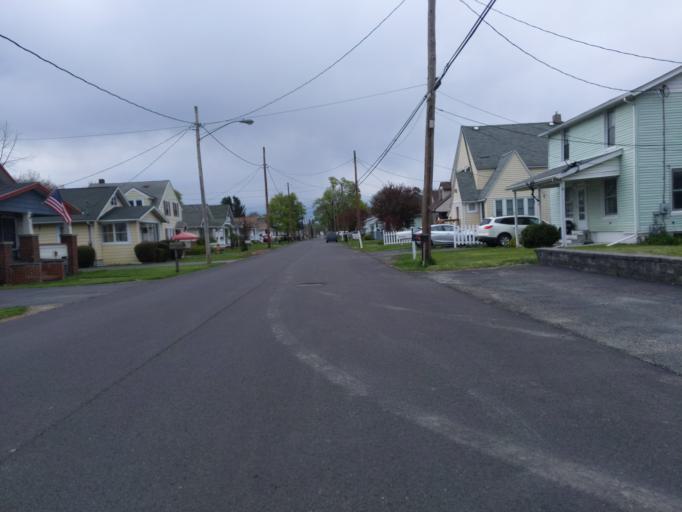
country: US
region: New York
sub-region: Chemung County
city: Southport
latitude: 42.0633
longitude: -76.8123
